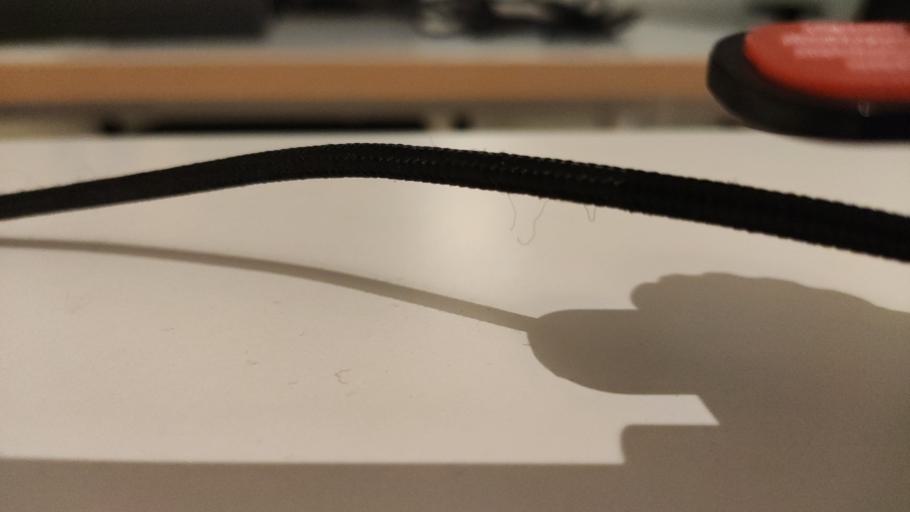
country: RU
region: Moskovskaya
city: Kurovskoye
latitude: 55.6051
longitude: 38.9271
